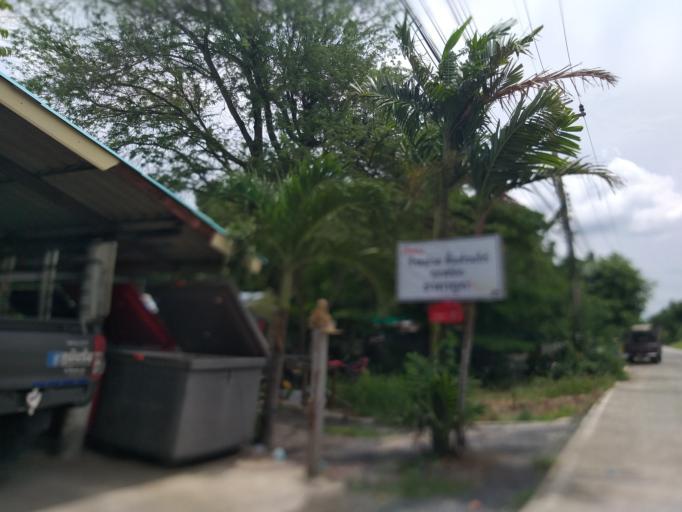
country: TH
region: Pathum Thani
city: Ban Lam Luk Ka
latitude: 13.9866
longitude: 100.8543
